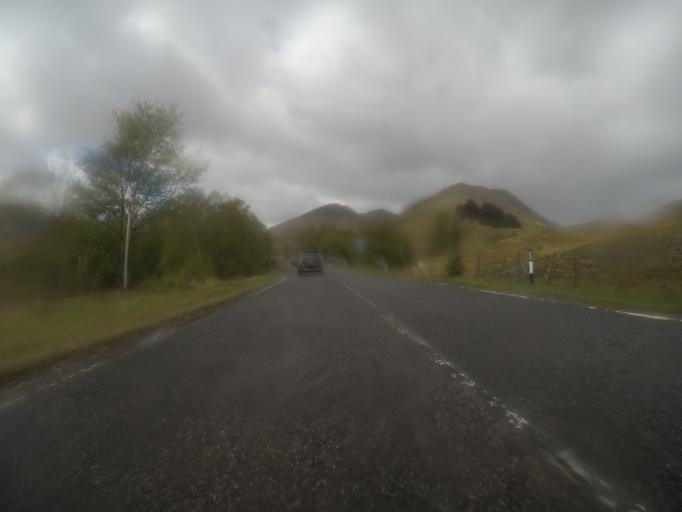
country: GB
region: Scotland
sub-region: Highland
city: Fort William
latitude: 57.1599
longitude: -5.1584
